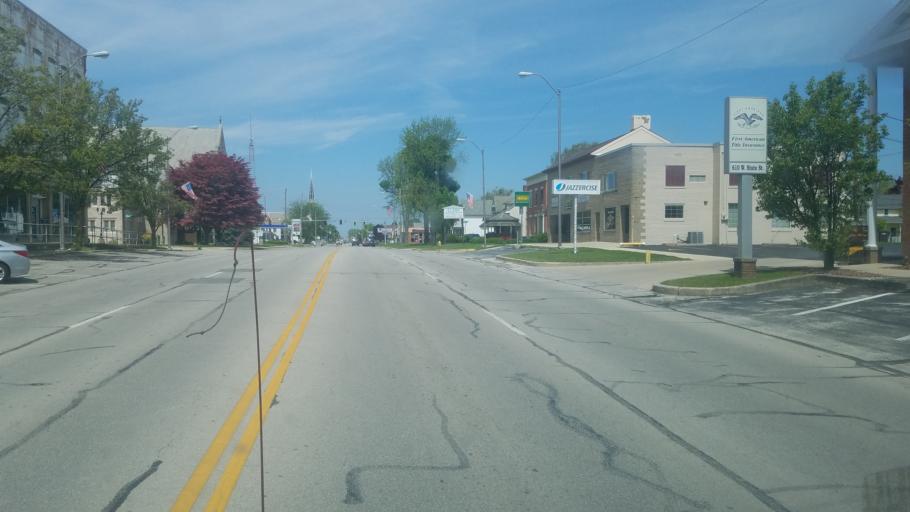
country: US
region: Ohio
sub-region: Sandusky County
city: Fremont
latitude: 41.3488
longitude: -83.1171
